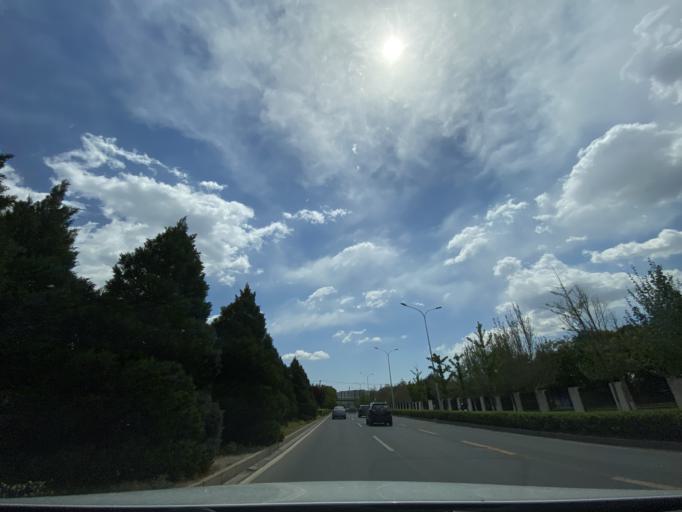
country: CN
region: Beijing
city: Sijiqing
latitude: 39.9366
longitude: 116.2421
